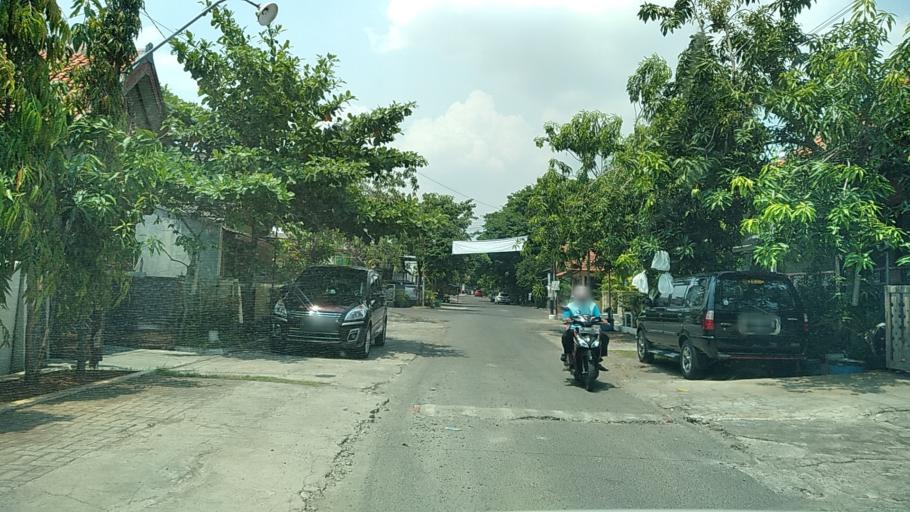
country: ID
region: Central Java
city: Mranggen
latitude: -7.0198
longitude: 110.4781
